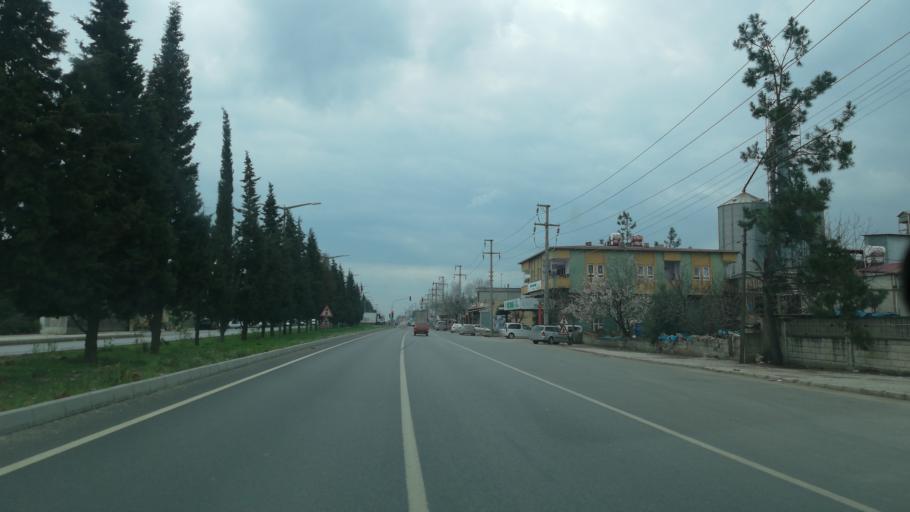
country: TR
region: Kahramanmaras
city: Turkoglu
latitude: 37.4141
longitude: 36.8801
